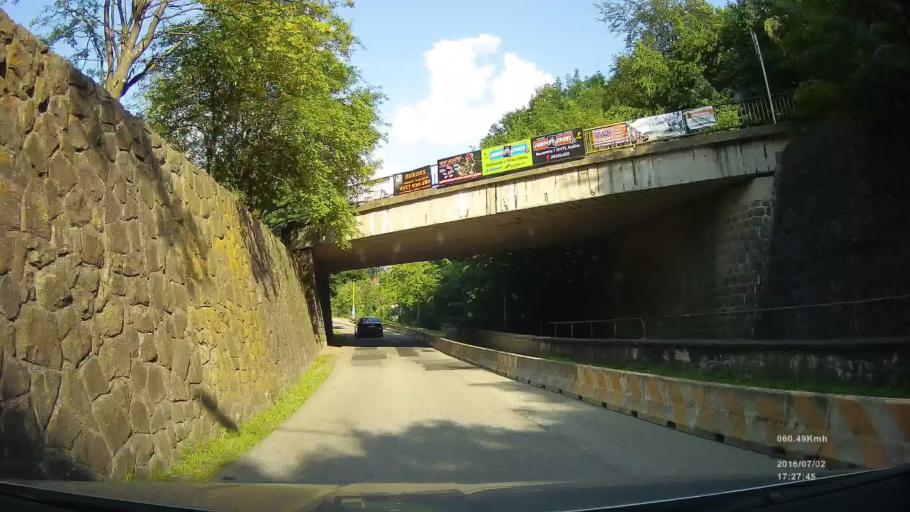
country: SK
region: Kosicky
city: Kosice
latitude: 48.7494
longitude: 21.2297
